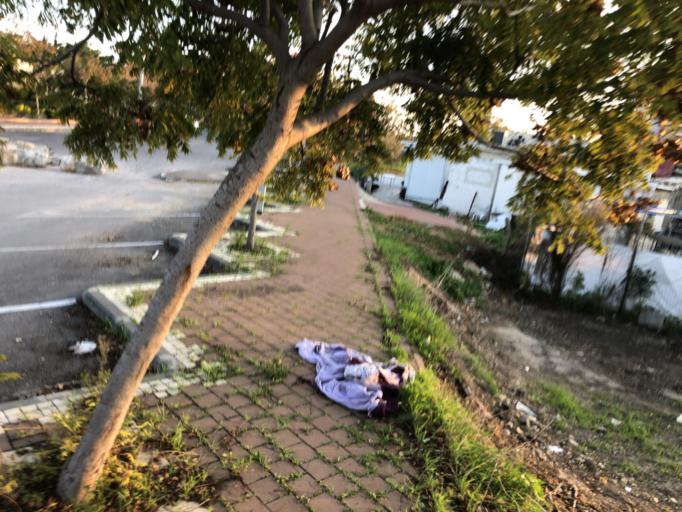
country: IL
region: Northern District
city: `Akko
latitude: 32.9310
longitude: 35.0826
